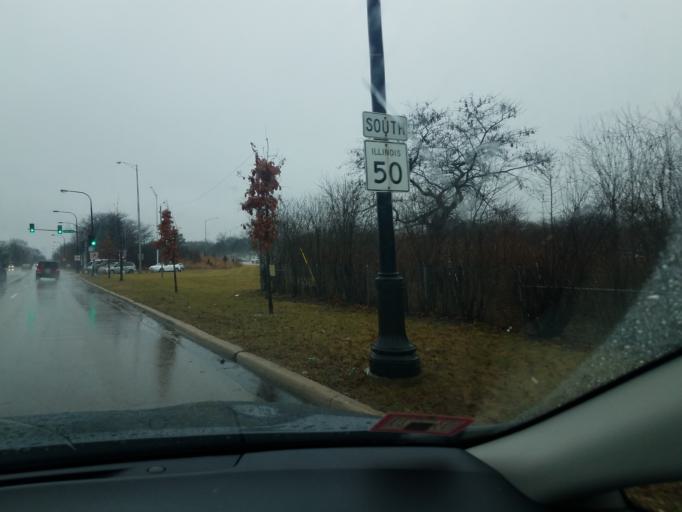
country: US
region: Illinois
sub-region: Cook County
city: Lincolnwood
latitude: 42.0107
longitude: -87.7481
